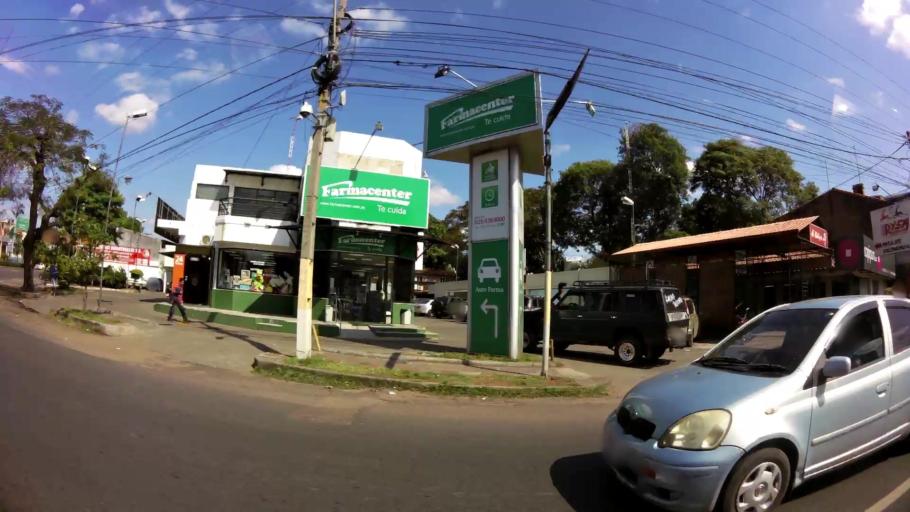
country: PY
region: Central
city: San Lorenzo
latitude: -25.3433
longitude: -57.5036
